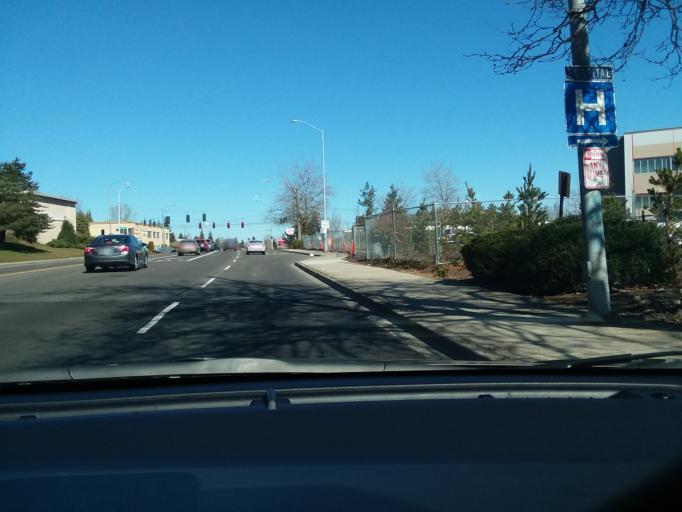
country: US
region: Washington
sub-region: Pierce County
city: Fircrest
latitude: 47.2418
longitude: -122.4824
